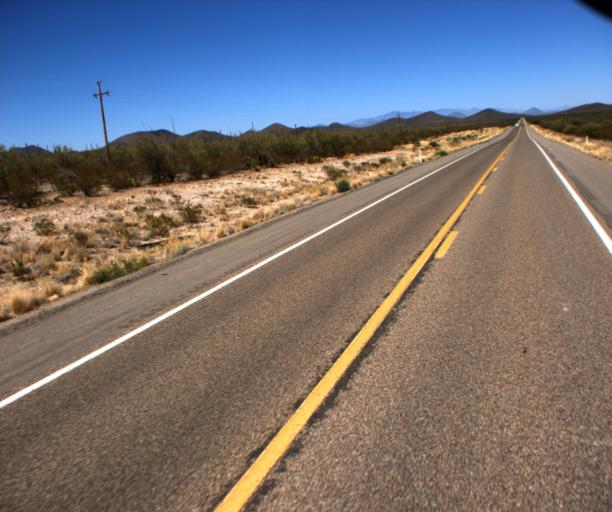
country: US
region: Arizona
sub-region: Pima County
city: Three Points
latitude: 32.0441
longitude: -111.4365
